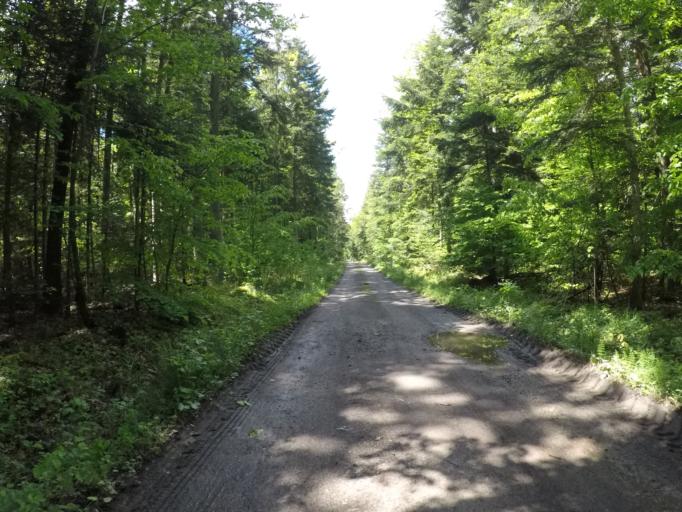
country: PL
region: Swietokrzyskie
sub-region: Powiat kielecki
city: Kostomloty Pierwsze
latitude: 50.9201
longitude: 20.6344
